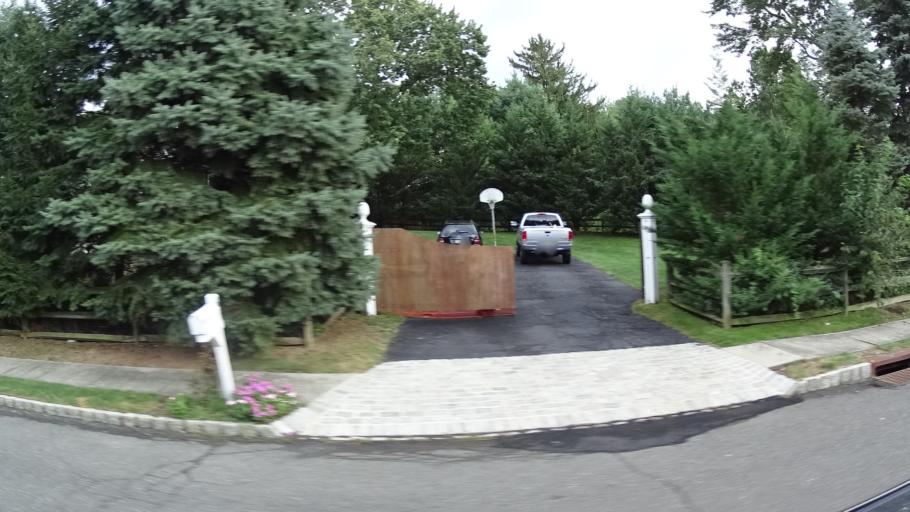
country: US
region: New Jersey
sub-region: Union County
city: Berkeley Heights
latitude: 40.6978
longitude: -74.4478
